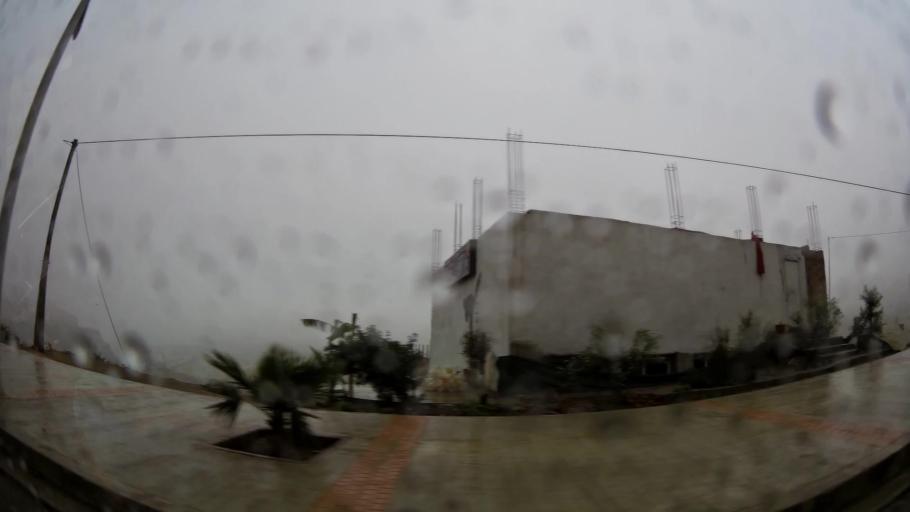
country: MA
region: Taza-Al Hoceima-Taounate
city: Tirhanimine
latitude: 35.2365
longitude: -3.9414
